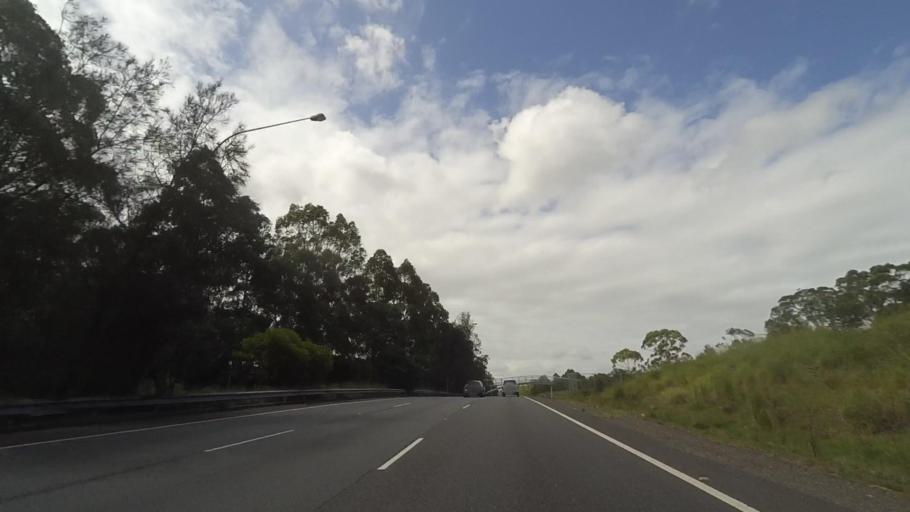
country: AU
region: New South Wales
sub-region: Newcastle
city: North Lambton
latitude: -32.9049
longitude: 151.6927
